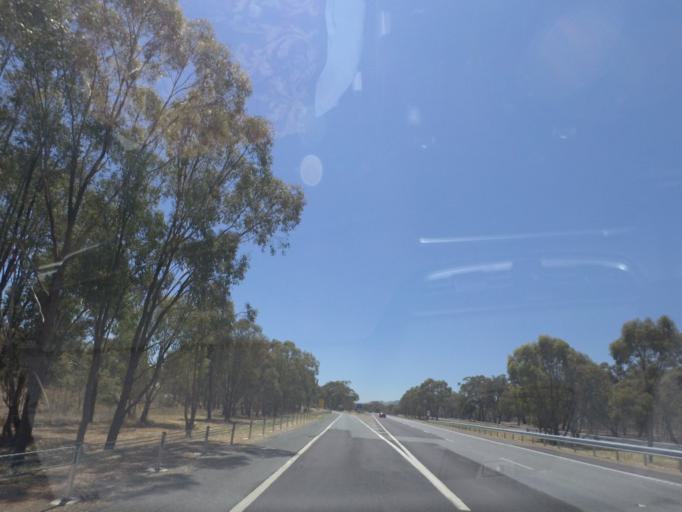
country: AU
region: Victoria
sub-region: Benalla
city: Benalla
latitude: -36.7161
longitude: 145.6328
